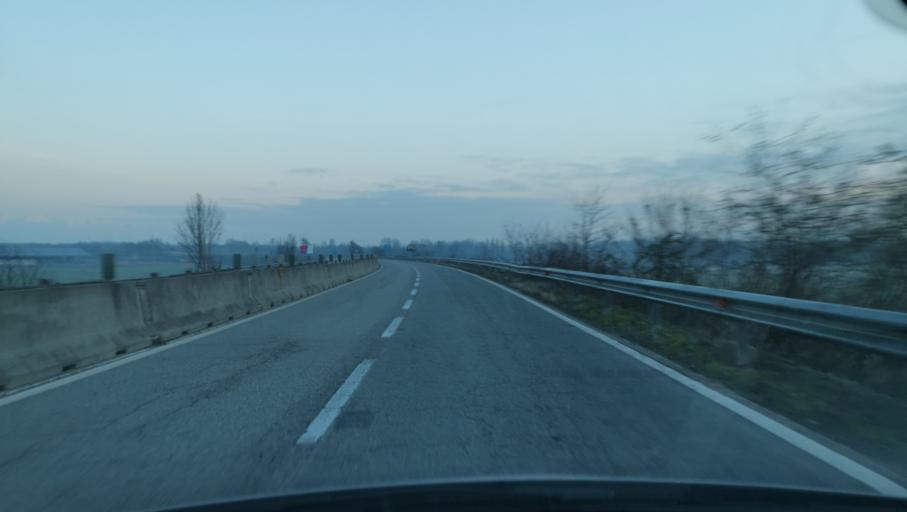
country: IT
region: Piedmont
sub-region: Provincia di Torino
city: Brandizzo
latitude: 45.1804
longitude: 7.8581
